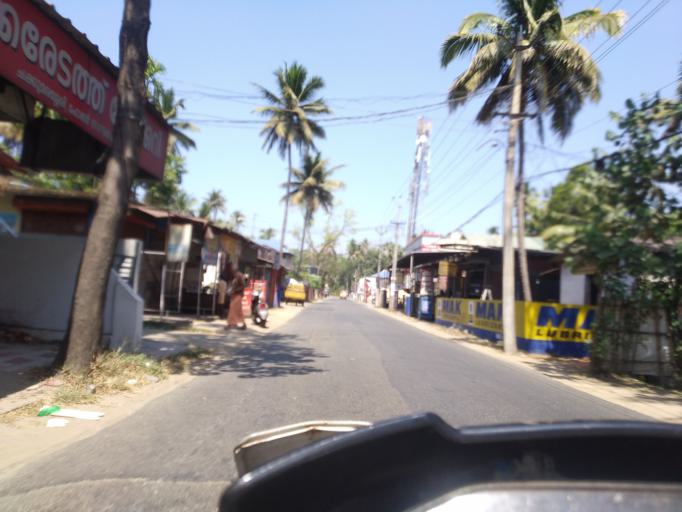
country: IN
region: Kerala
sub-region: Thrissur District
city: Kodungallur
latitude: 10.1665
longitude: 76.2132
